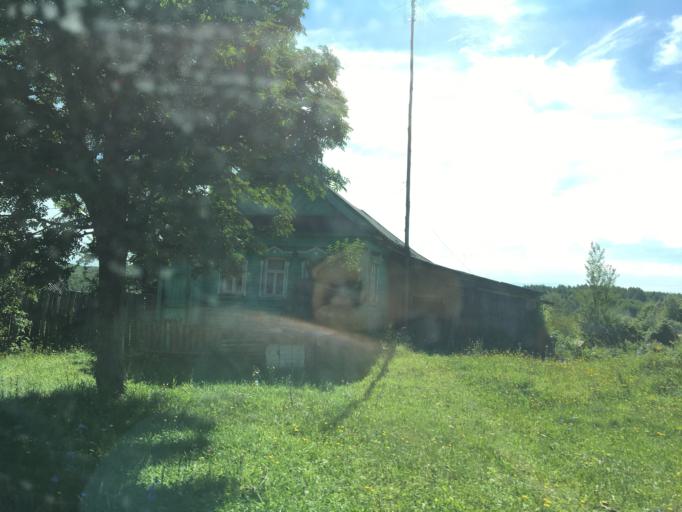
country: RU
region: Nizjnij Novgorod
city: Lyskovo
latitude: 55.9862
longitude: 45.0400
